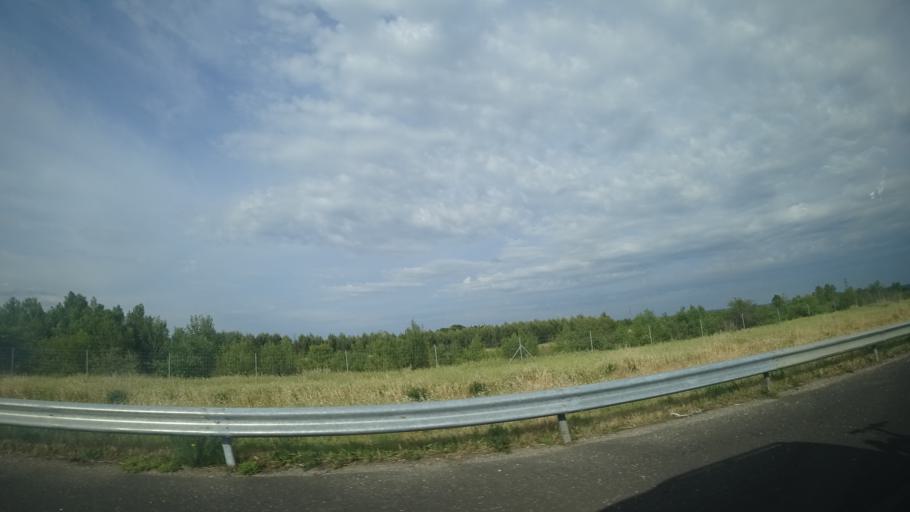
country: FR
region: Languedoc-Roussillon
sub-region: Departement de l'Herault
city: Nebian
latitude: 43.6187
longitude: 3.4582
